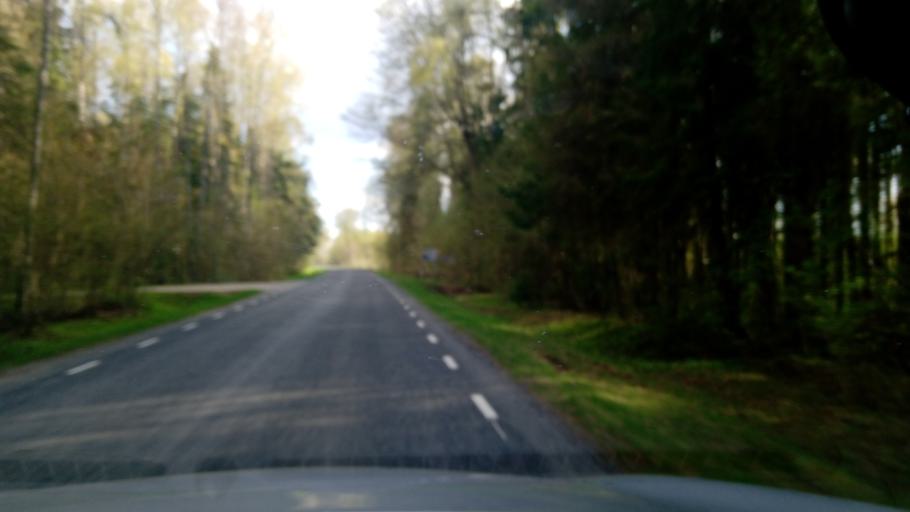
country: EE
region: Laeaene-Virumaa
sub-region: Tamsalu vald
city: Tamsalu
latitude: 59.1940
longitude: 26.1315
